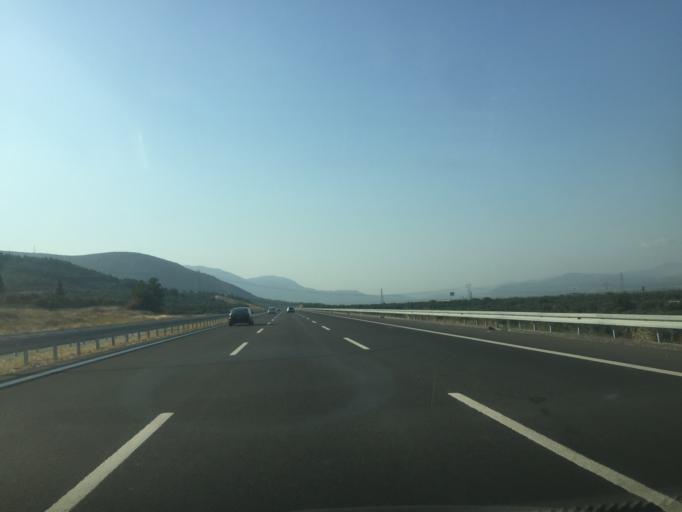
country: TR
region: Manisa
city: Kirkagac
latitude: 39.0526
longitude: 27.7313
